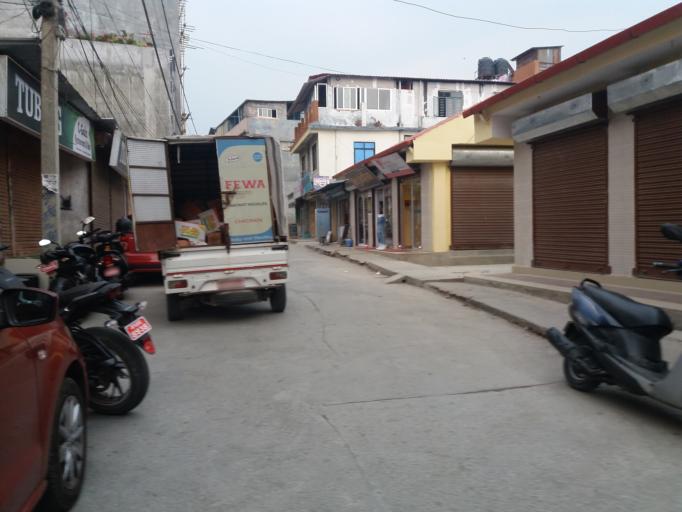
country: NP
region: Western Region
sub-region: Gandaki Zone
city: Pokhara
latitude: 28.2221
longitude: 83.9884
